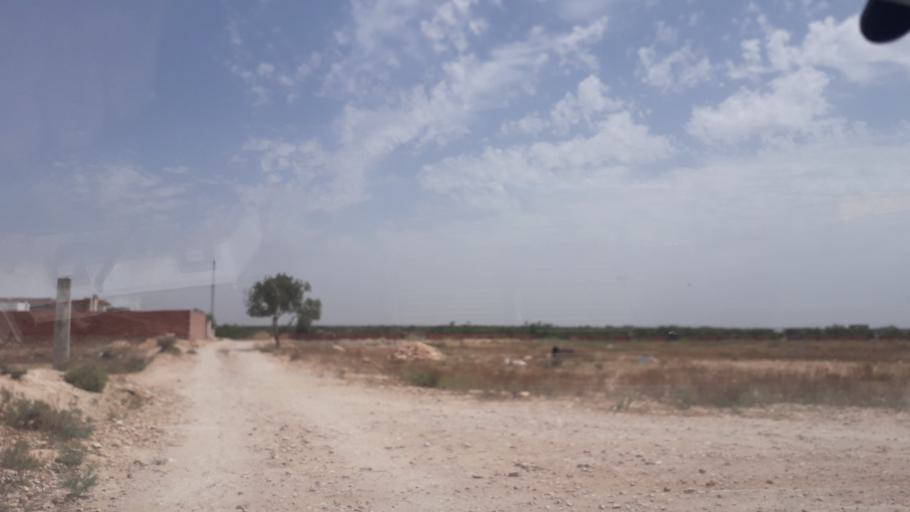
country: TN
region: Safaqis
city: Al Qarmadah
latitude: 34.8462
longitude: 10.7740
